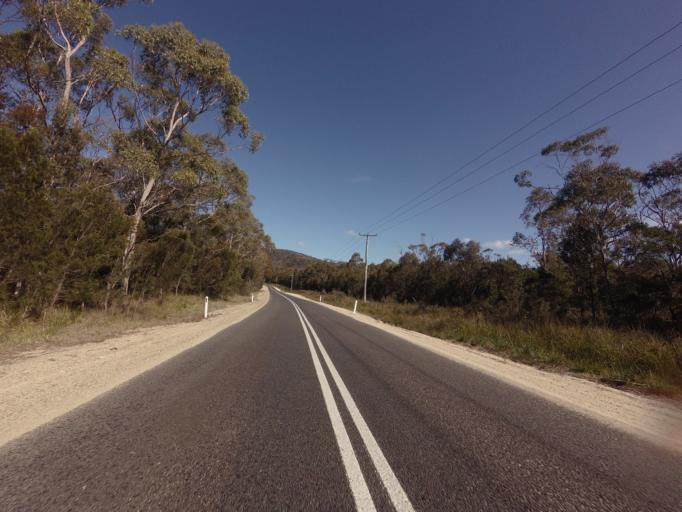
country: AU
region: Tasmania
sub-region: Break O'Day
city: St Helens
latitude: -41.8433
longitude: 148.2547
